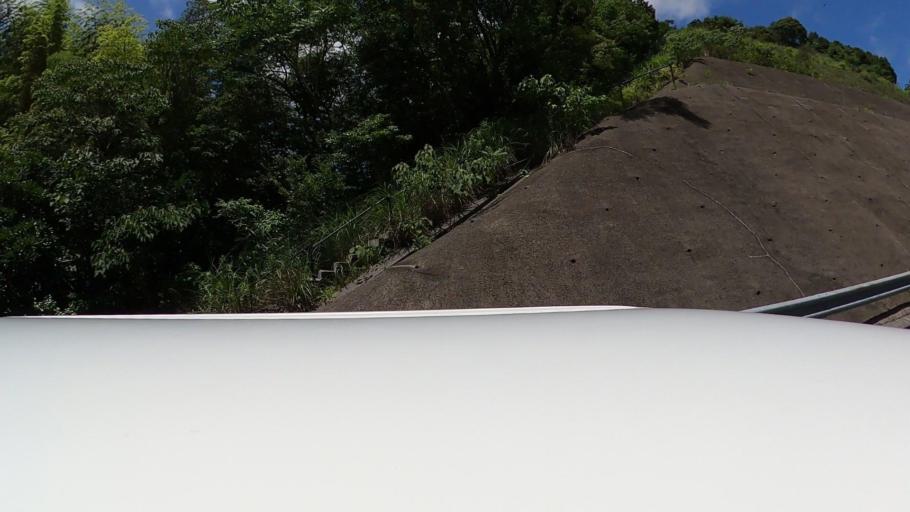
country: JP
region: Miyazaki
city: Nobeoka
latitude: 32.4944
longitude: 131.6567
